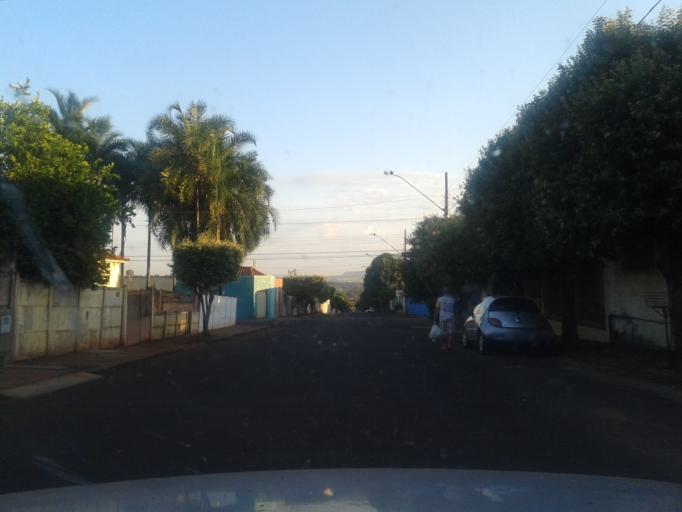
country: BR
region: Minas Gerais
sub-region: Ituiutaba
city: Ituiutaba
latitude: -18.9812
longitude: -49.4672
